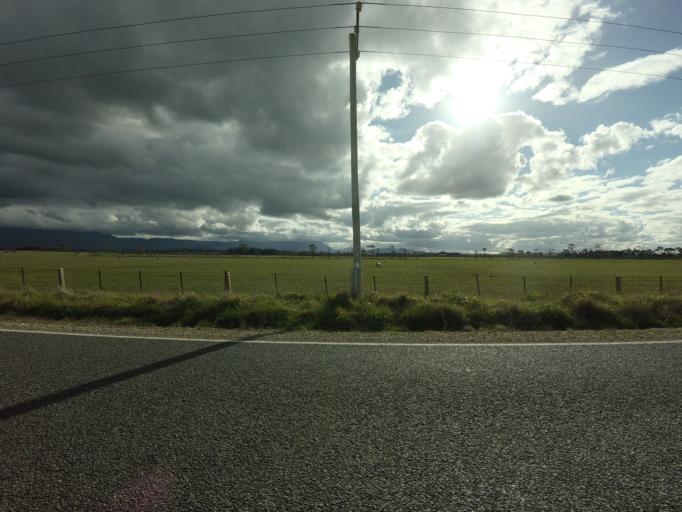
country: AU
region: Tasmania
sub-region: Northern Midlands
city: Longford
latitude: -41.7370
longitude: 147.0841
